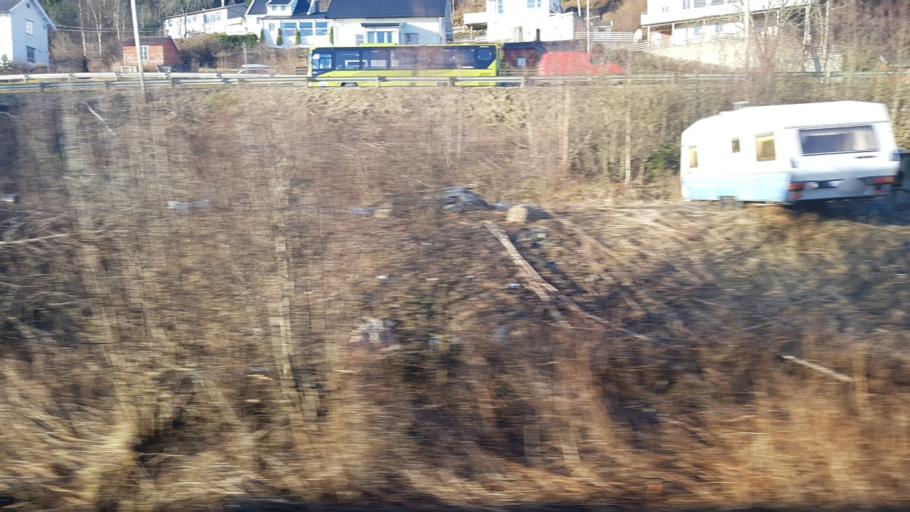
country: NO
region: Sor-Trondelag
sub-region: Malvik
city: Hommelvik
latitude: 63.4238
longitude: 10.7648
